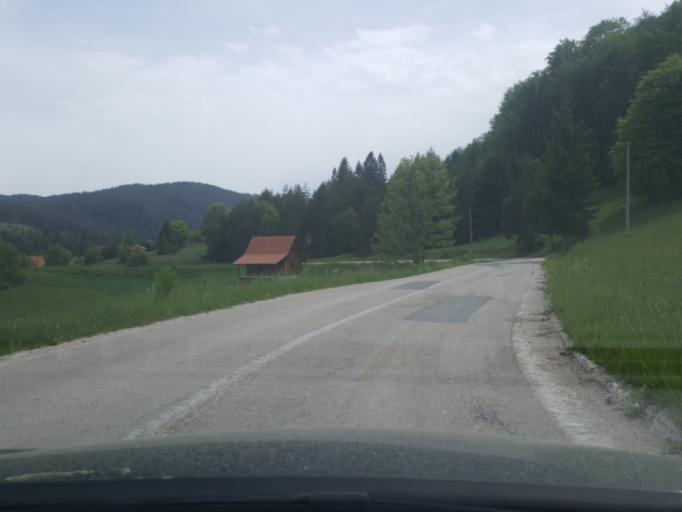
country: RS
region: Central Serbia
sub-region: Zlatiborski Okrug
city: Bajina Basta
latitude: 43.8945
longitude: 19.5217
